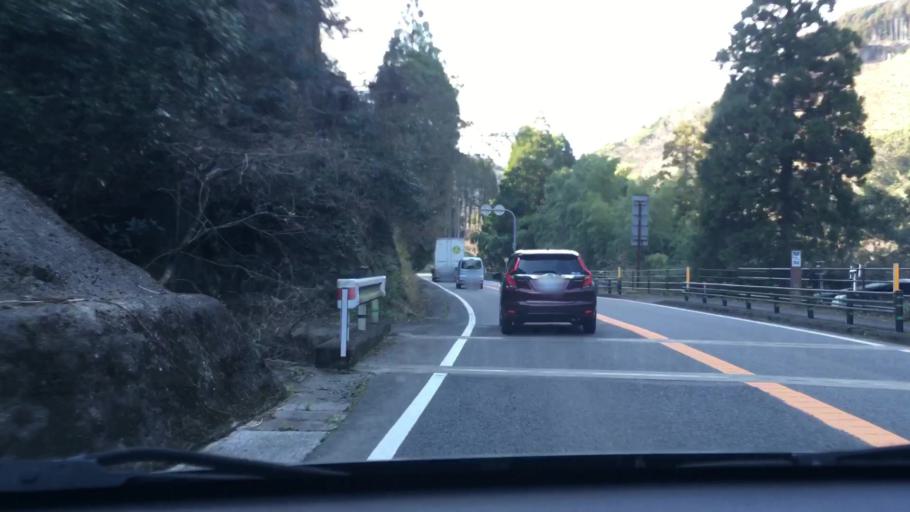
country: JP
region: Oita
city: Tsukumiura
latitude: 33.0004
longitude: 131.8118
